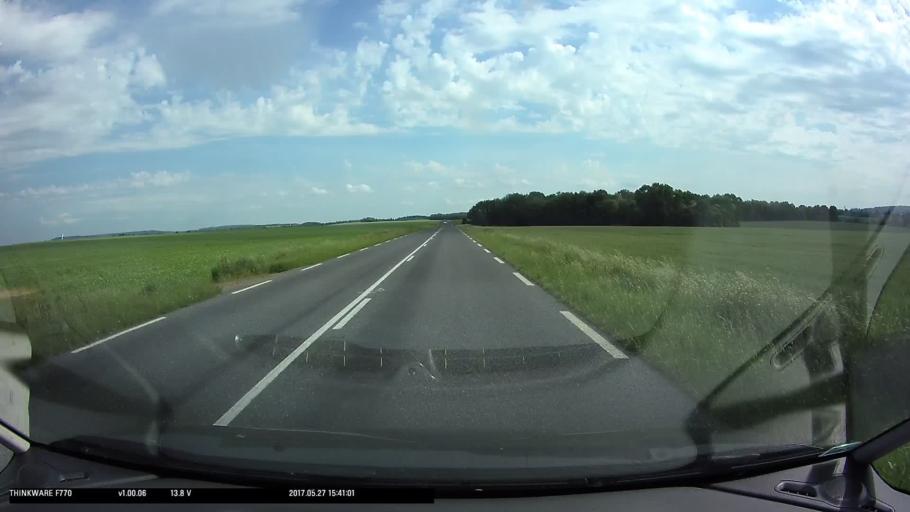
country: FR
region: Picardie
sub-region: Departement de l'Oise
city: Chaumont-en-Vexin
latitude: 49.2357
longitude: 1.8786
